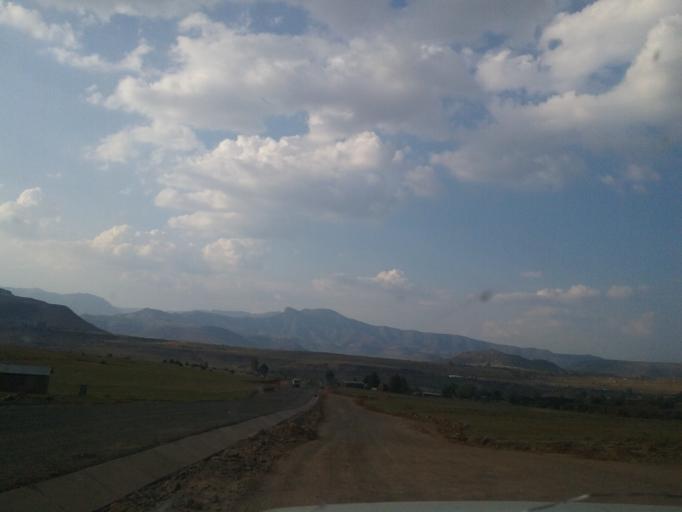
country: LS
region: Quthing
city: Quthing
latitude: -30.4016
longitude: 27.6106
